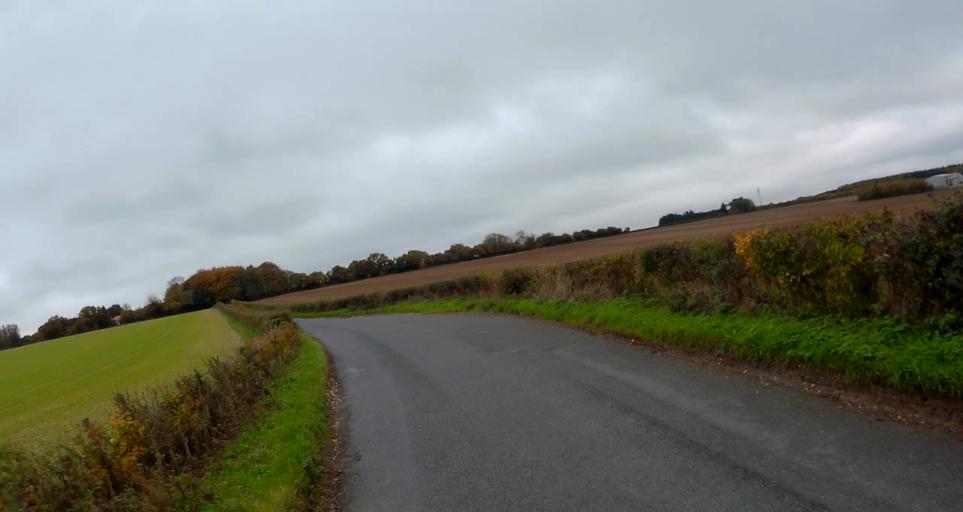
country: GB
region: England
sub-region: Hampshire
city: Basingstoke
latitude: 51.2250
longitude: -1.1254
